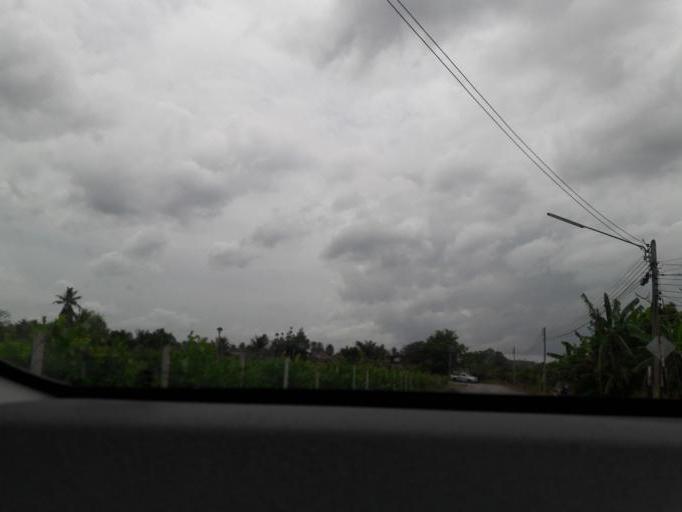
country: TH
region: Ratchaburi
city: Damnoen Saduak
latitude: 13.5695
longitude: 99.9817
